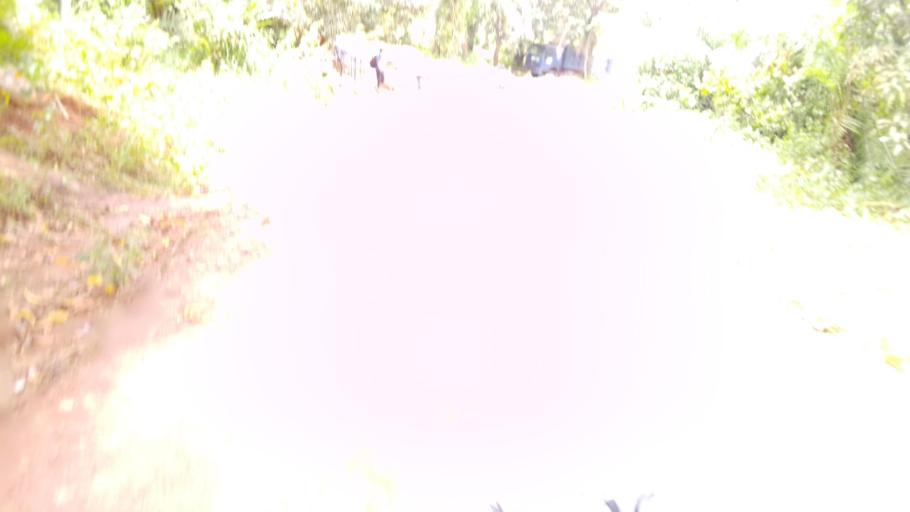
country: SL
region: Eastern Province
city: Koidu
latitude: 8.6735
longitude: -10.9385
